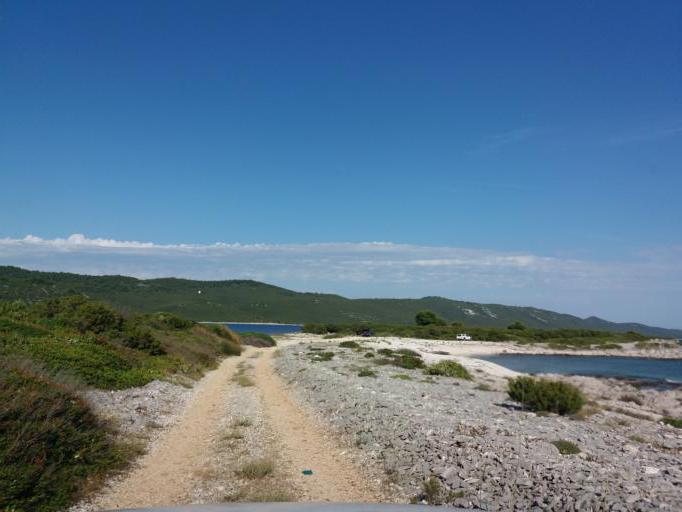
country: HR
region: Zadarska
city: Ugljan
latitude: 44.1256
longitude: 14.8711
